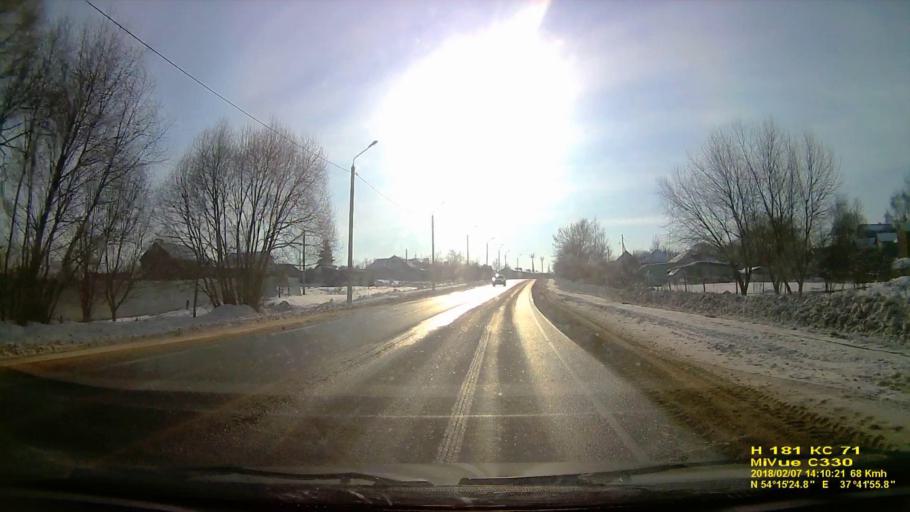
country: RU
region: Tula
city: Gorelki
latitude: 54.2568
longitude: 37.6988
